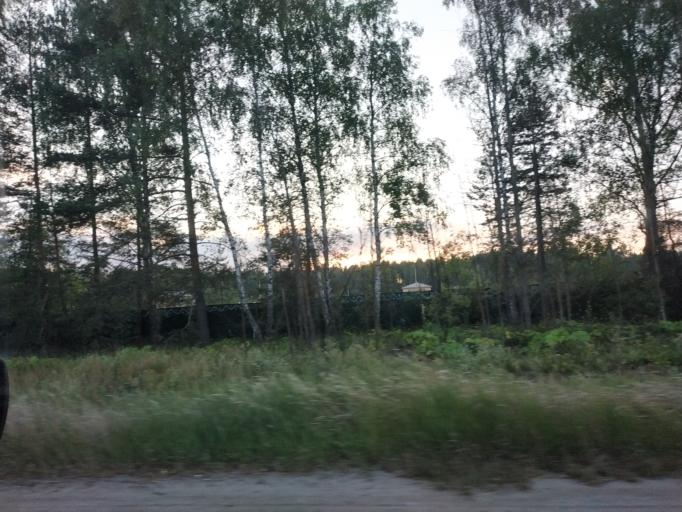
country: RU
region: Moskovskaya
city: Krasnoarmeysk
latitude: 56.0527
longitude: 38.2312
